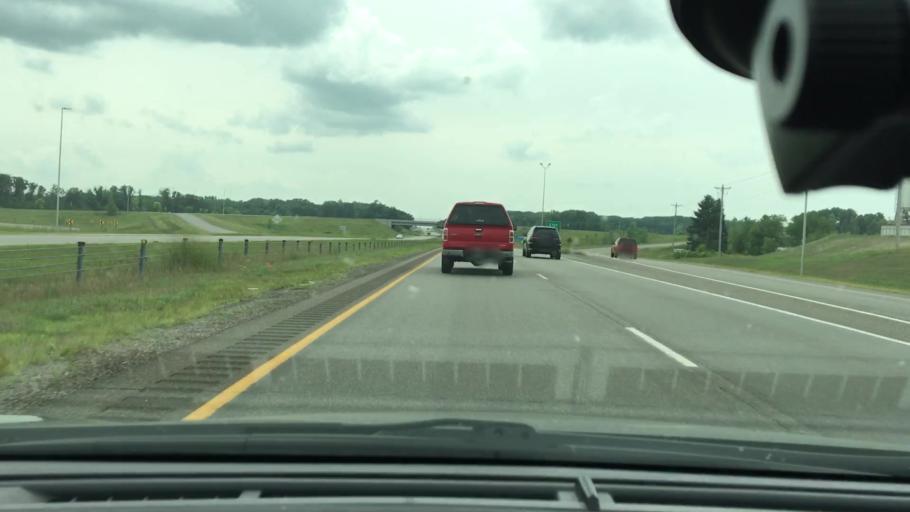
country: US
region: Minnesota
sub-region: Sherburne County
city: Elk River
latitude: 45.3472
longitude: -93.5588
